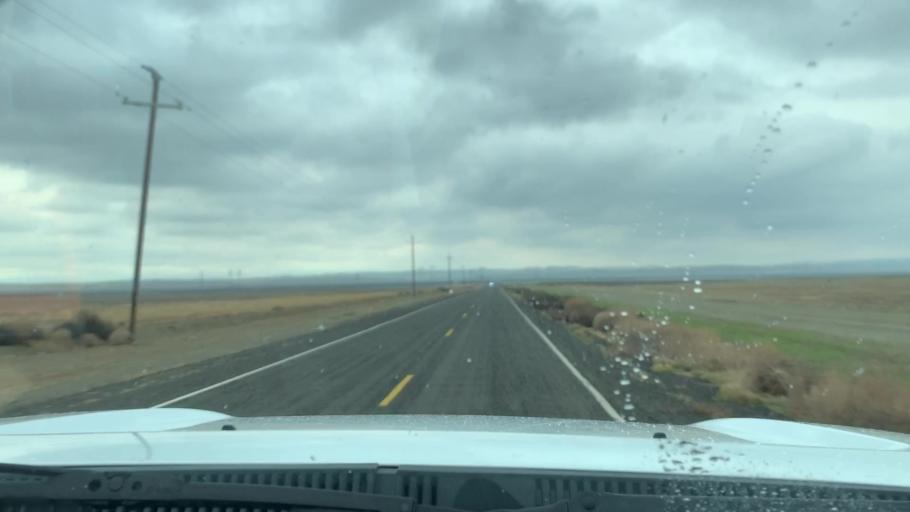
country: US
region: California
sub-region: Kings County
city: Kettleman City
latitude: 35.9343
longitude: -119.8804
